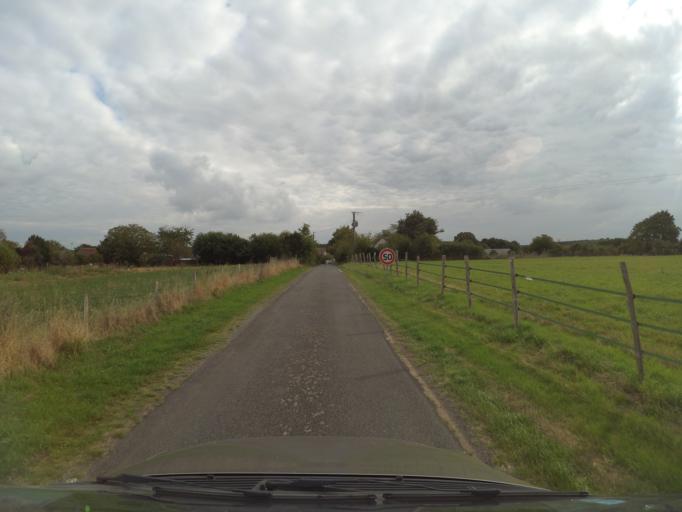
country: FR
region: Centre
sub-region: Departement d'Indre-et-Loire
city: Poce-sur-Cisse
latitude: 47.4876
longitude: 0.9772
